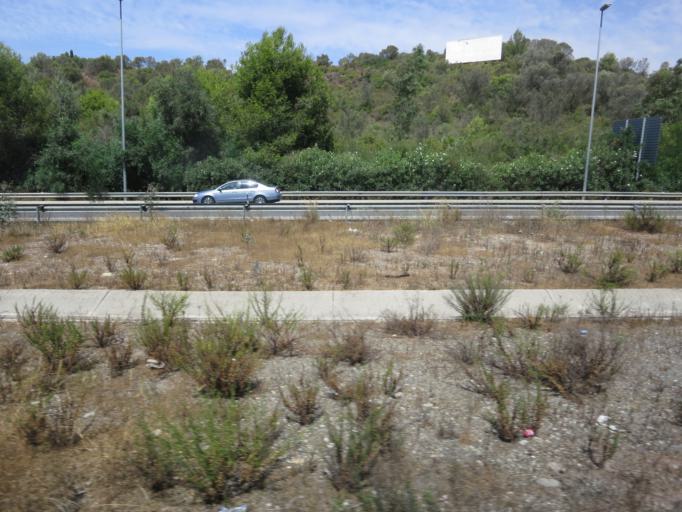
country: ES
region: Andalusia
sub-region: Provincia de Malaga
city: Marbella
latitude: 36.5132
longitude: -4.9436
